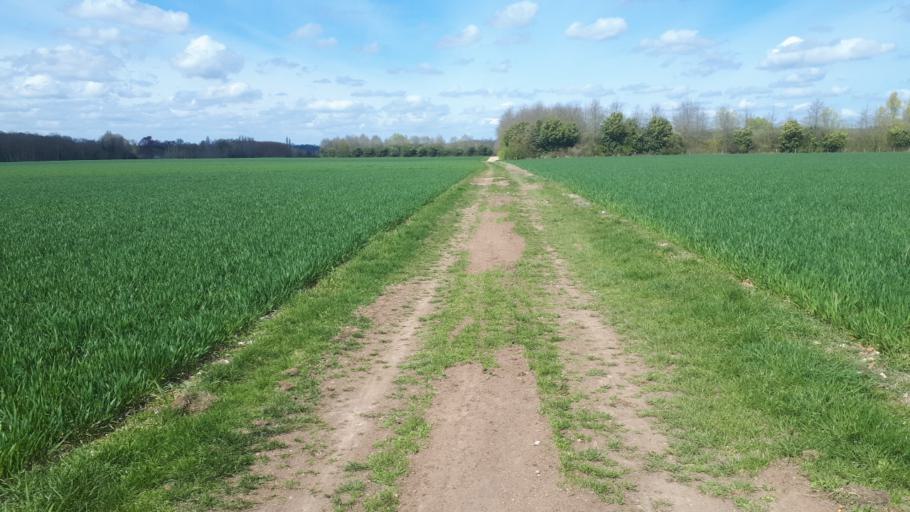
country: FR
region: Centre
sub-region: Departement du Loir-et-Cher
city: Villiers-sur-Loir
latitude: 47.7931
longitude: 0.9937
